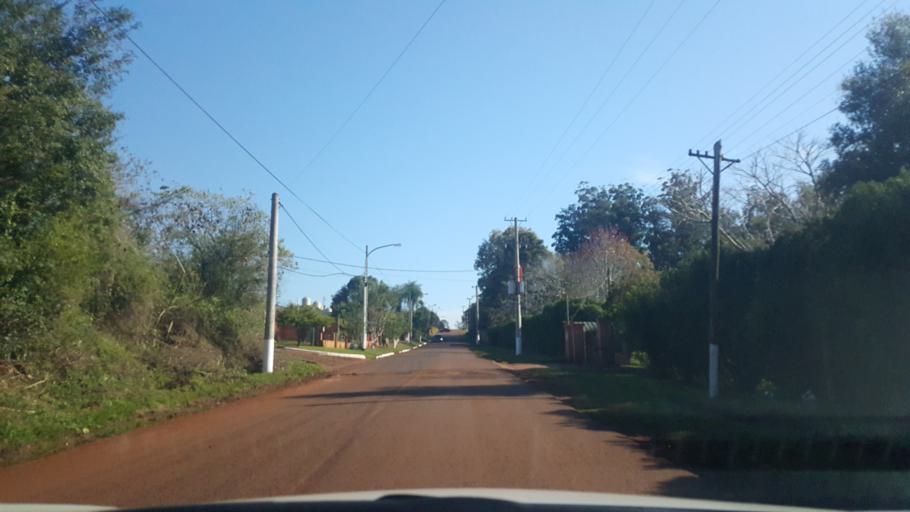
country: AR
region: Misiones
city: Santo Pipo
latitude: -27.1530
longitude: -55.3929
